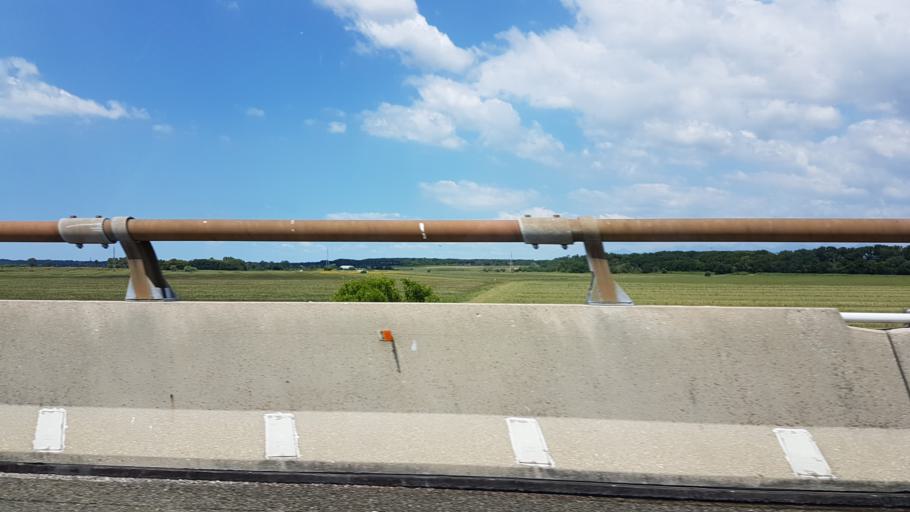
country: IT
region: Tuscany
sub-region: Provincia di Livorno
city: Guasticce
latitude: 43.6166
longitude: 10.3971
